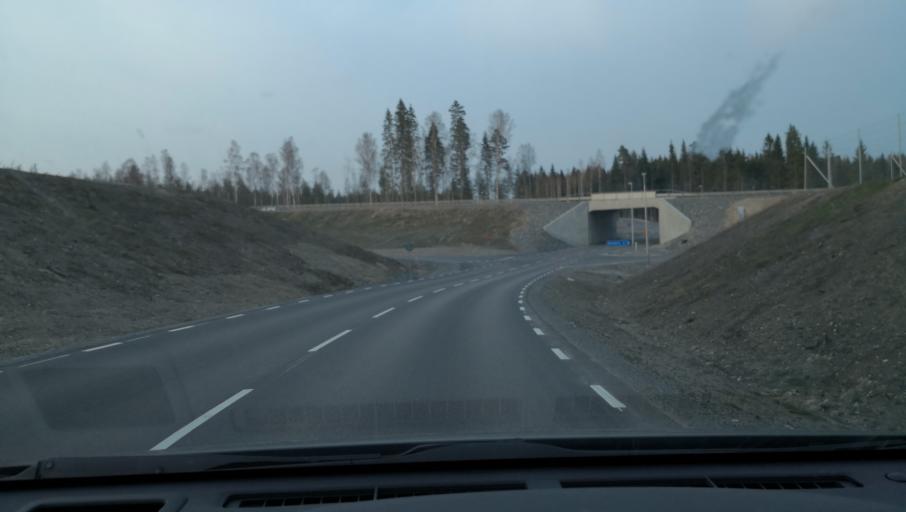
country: SE
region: OErebro
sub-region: Orebro Kommun
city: Hovsta
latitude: 59.4422
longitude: 15.1405
